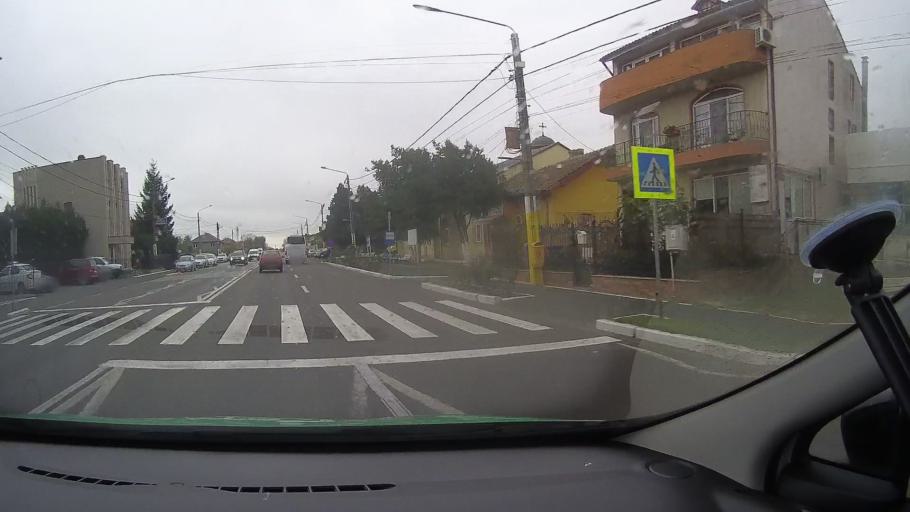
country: RO
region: Constanta
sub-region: Comuna Valu lui Traian
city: Valu lui Traian
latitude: 44.1647
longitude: 28.4797
